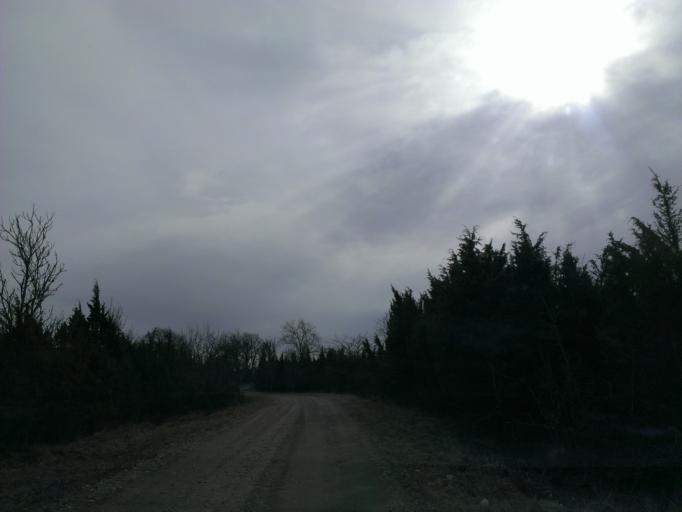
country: EE
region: Laeaene
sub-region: Lihula vald
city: Lihula
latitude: 58.5666
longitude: 23.5468
